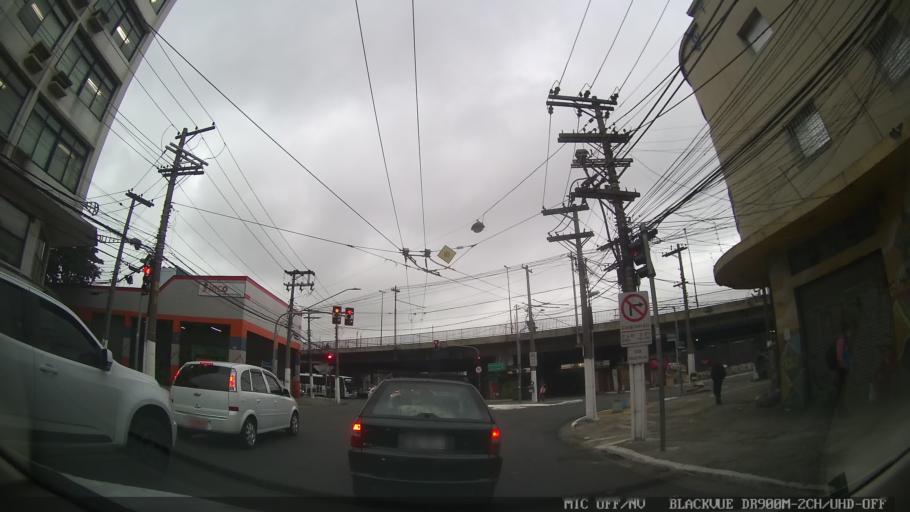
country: BR
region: Sao Paulo
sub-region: Sao Paulo
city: Sao Paulo
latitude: -23.5534
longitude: -46.5714
